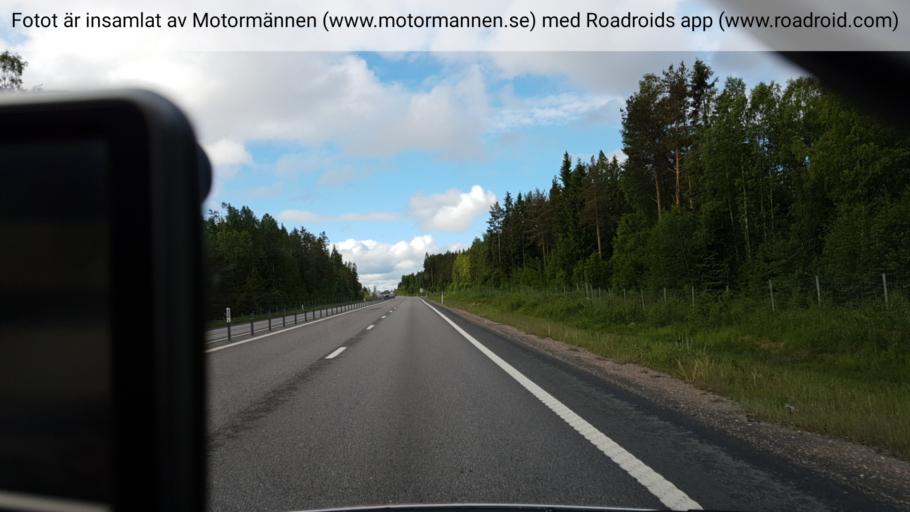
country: SE
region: Vaesternorrland
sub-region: Sundsvalls Kommun
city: Njurundabommen
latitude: 62.1257
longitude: 17.3332
